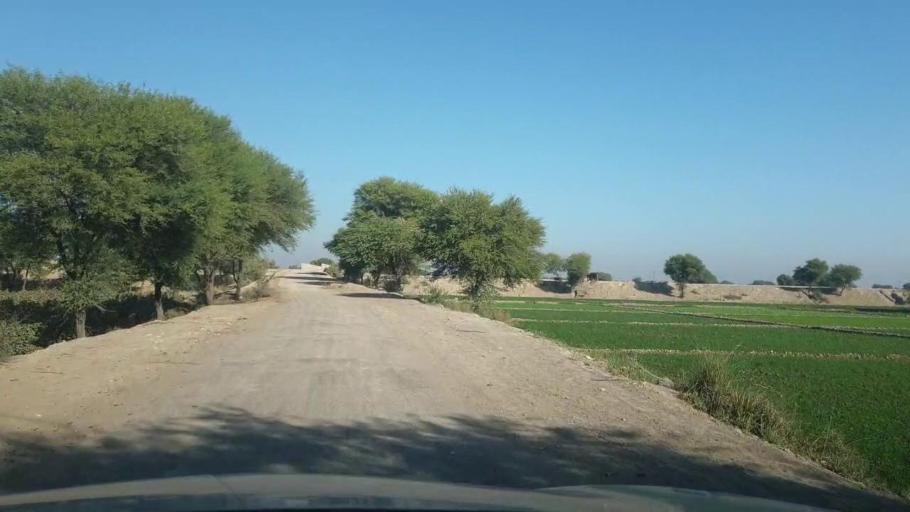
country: PK
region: Sindh
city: Bhan
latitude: 26.5571
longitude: 67.6641
